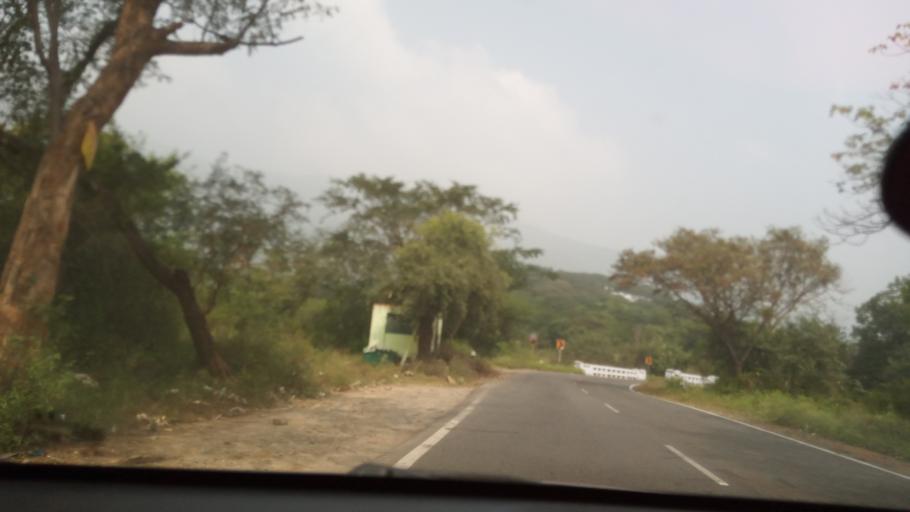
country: IN
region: Tamil Nadu
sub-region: Erode
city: Sathyamangalam
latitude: 11.5816
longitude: 77.1326
